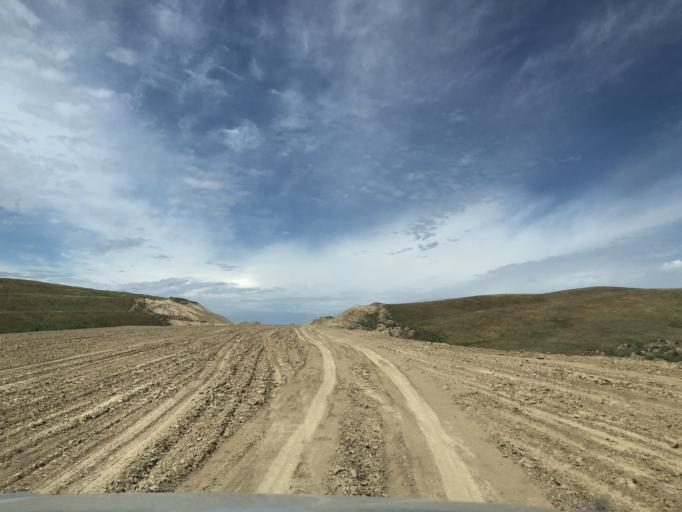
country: KZ
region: Almaty Oblysy
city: Burunday
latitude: 43.2963
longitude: 76.2186
